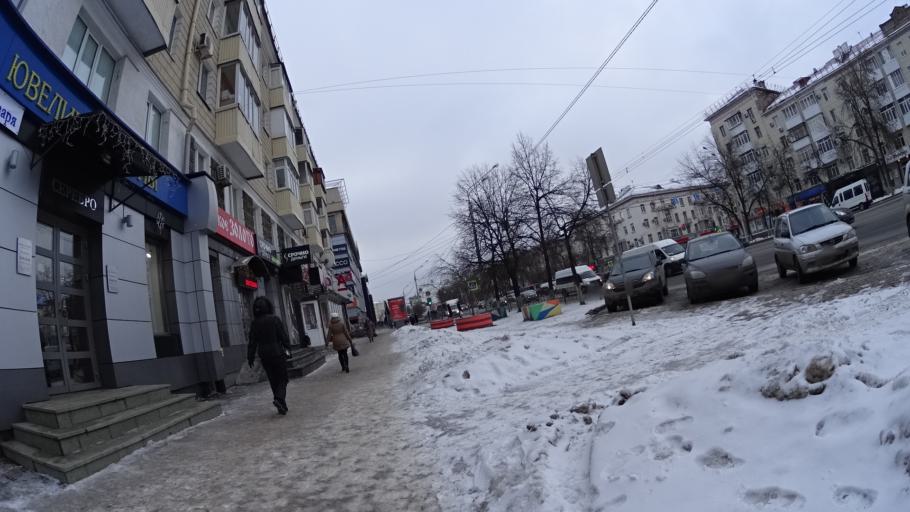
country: RU
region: Bashkortostan
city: Ufa
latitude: 54.7425
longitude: 55.9895
